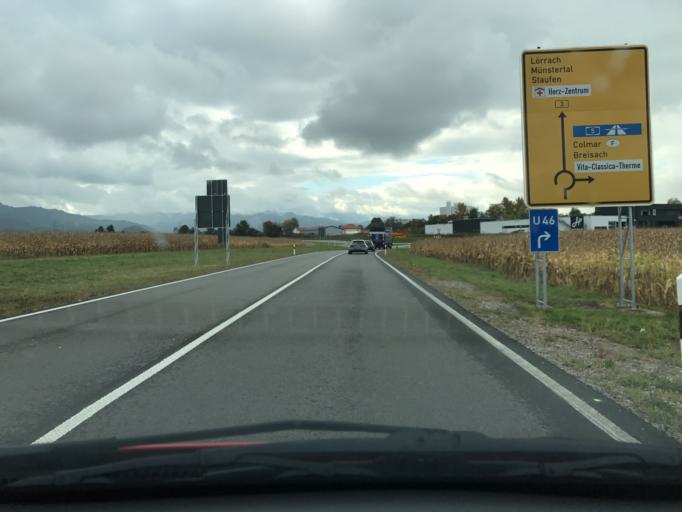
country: DE
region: Baden-Wuerttemberg
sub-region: Freiburg Region
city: Bad Krozingen
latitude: 47.9237
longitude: 7.7108
